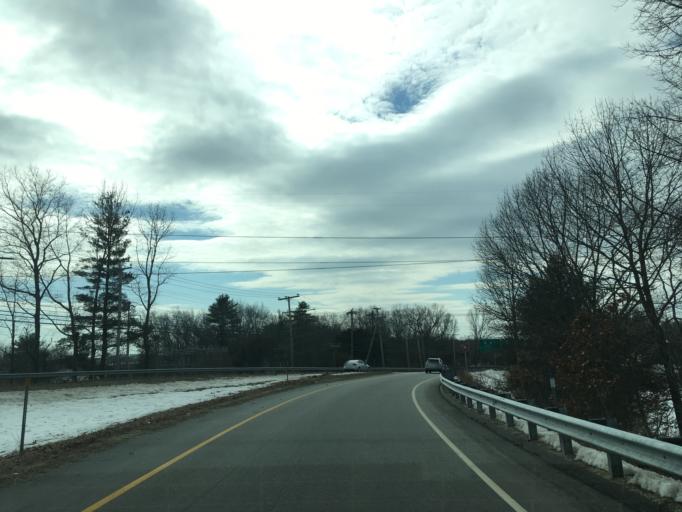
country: US
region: New Hampshire
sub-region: Rockingham County
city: Hampton
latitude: 42.9321
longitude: -70.8429
